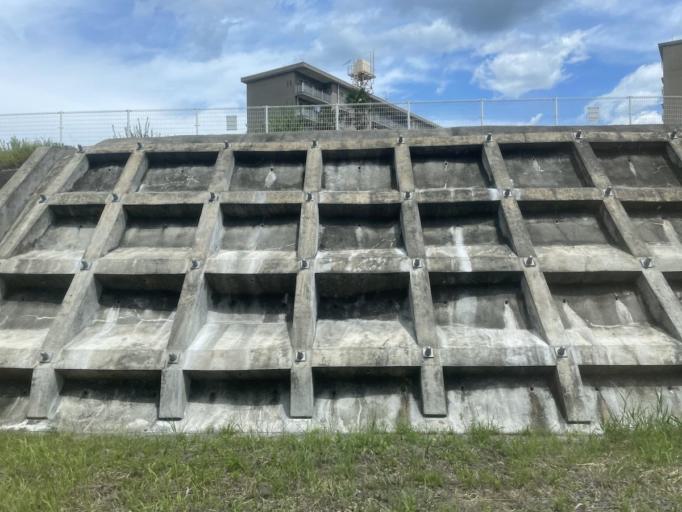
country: JP
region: Saitama
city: Chichibu
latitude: 35.9777
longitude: 139.1052
